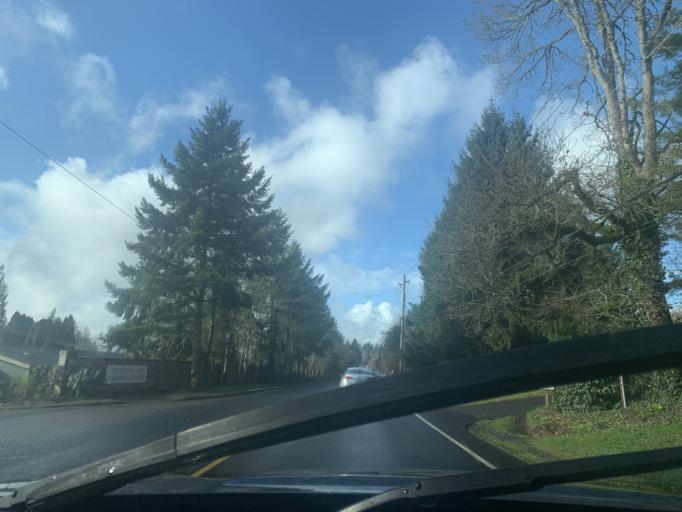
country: US
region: Oregon
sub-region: Washington County
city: King City
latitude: 45.4038
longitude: -122.8154
